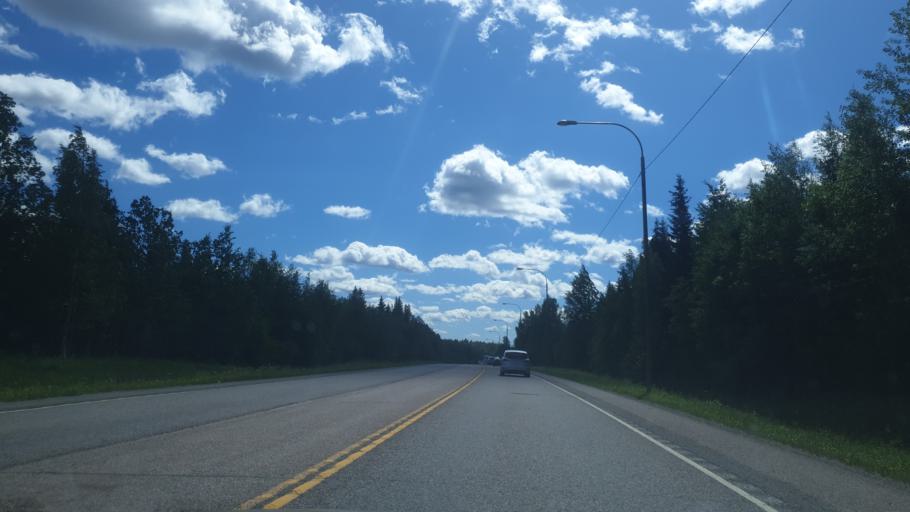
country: FI
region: Northern Savo
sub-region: Varkaus
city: Varkaus
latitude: 62.3593
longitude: 27.8112
